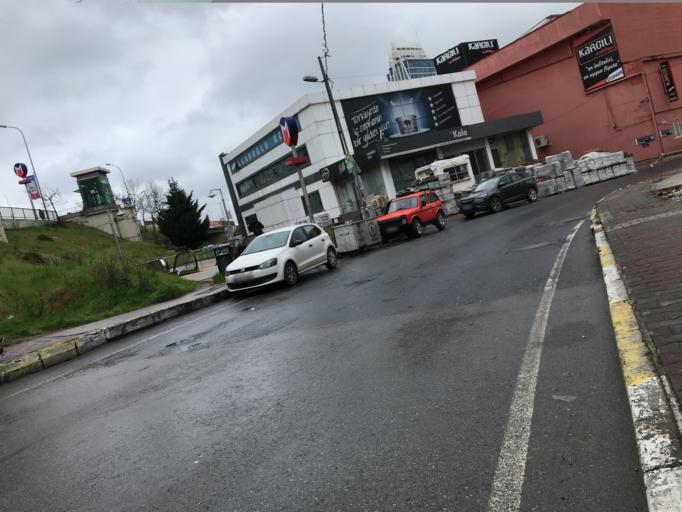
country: TR
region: Istanbul
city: Maltepe
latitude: 40.9369
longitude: 29.1398
